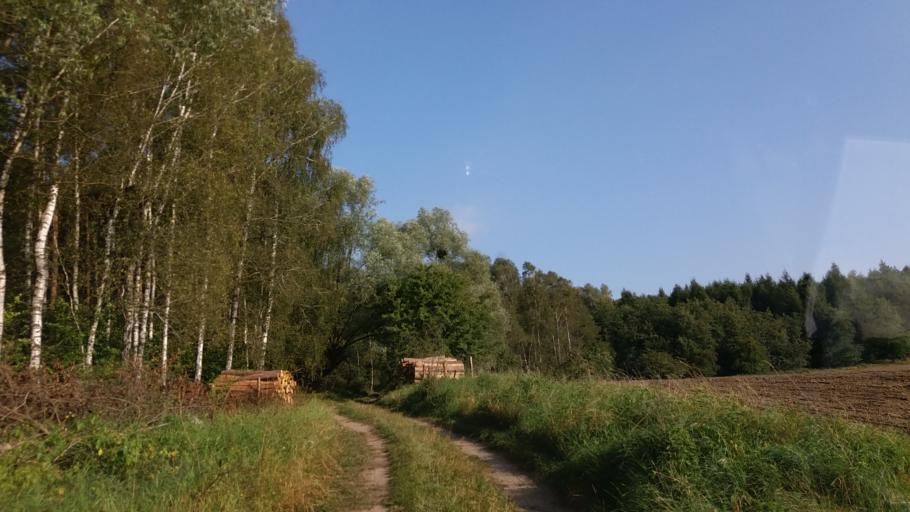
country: PL
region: West Pomeranian Voivodeship
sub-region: Powiat choszczenski
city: Recz
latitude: 53.1912
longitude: 15.5414
